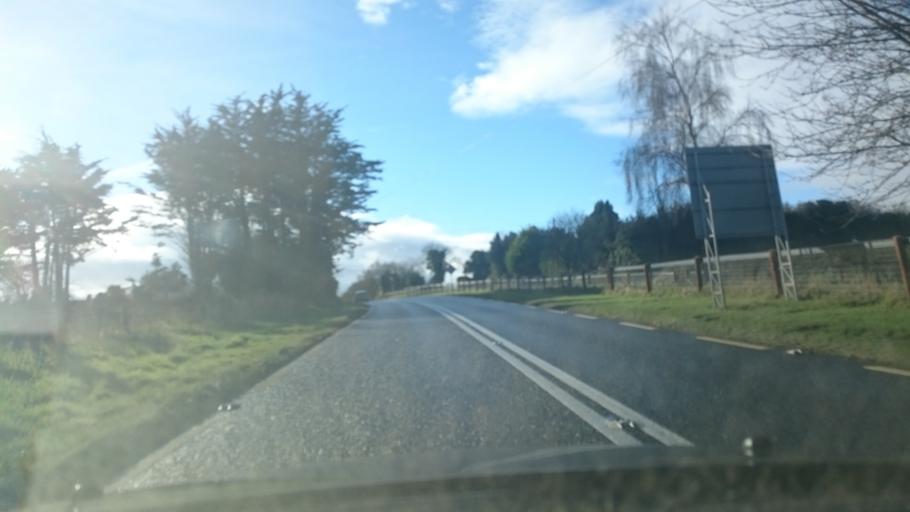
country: IE
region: Leinster
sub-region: Kilkenny
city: Kilkenny
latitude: 52.5903
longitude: -7.3101
